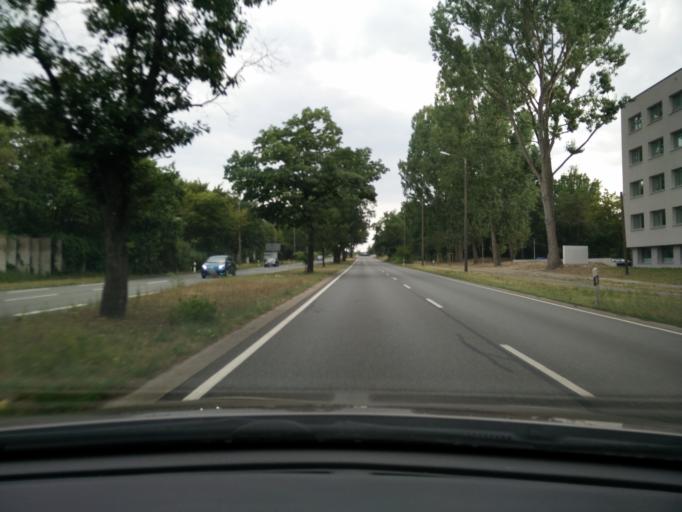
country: DE
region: Bavaria
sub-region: Regierungsbezirk Mittelfranken
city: Nuernberg
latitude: 49.4115
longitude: 11.1131
